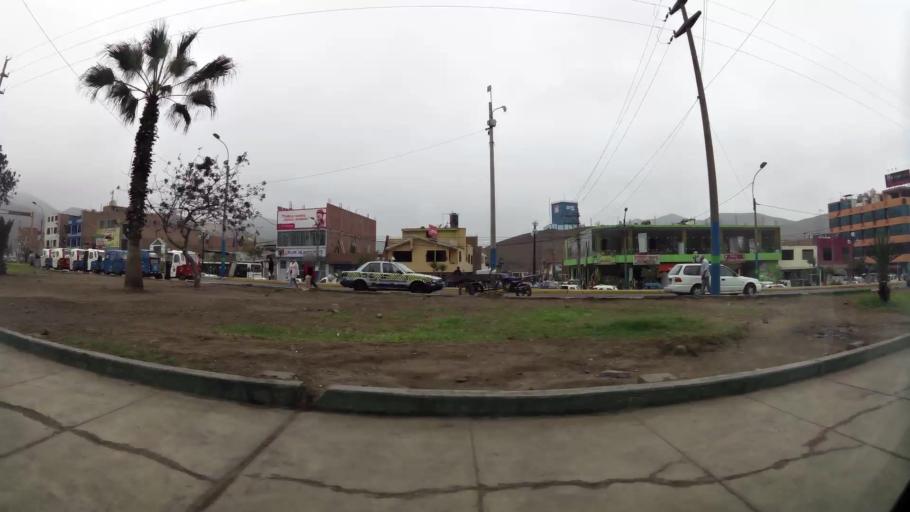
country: PE
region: Lima
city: Ventanilla
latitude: -11.8776
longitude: -77.1291
